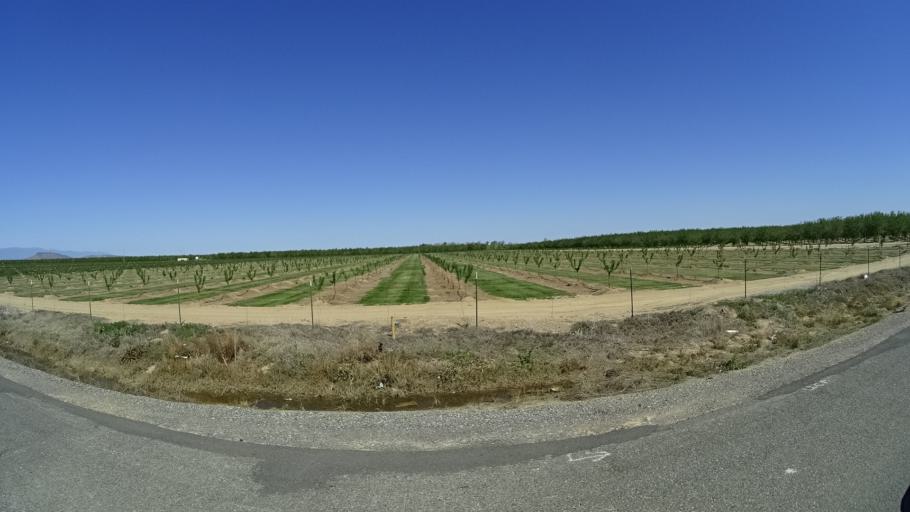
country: US
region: California
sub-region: Glenn County
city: Orland
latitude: 39.6970
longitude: -122.2403
